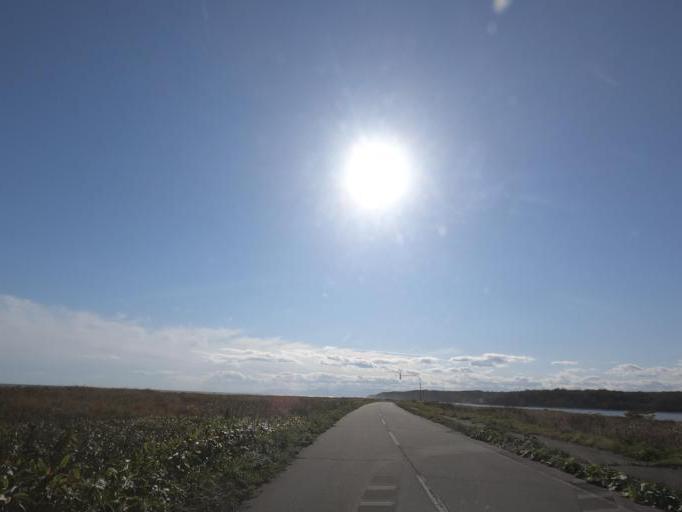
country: JP
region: Hokkaido
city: Obihiro
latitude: 42.5858
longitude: 143.5351
